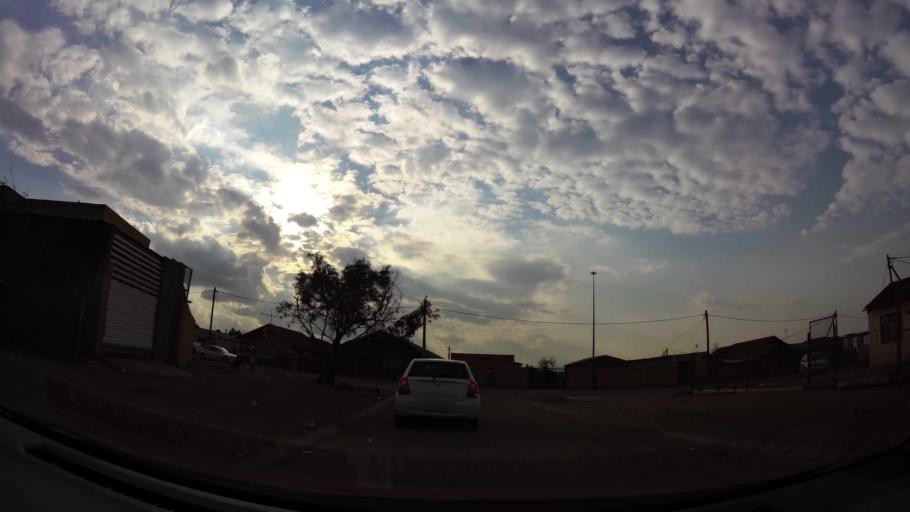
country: ZA
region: Gauteng
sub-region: Sedibeng District Municipality
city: Vanderbijlpark
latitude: -26.6751
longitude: 27.8721
